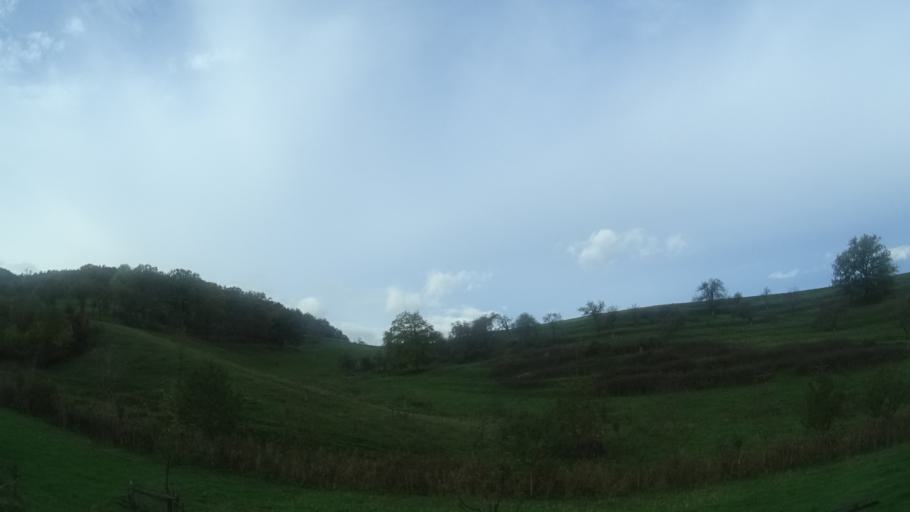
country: DE
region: Thuringia
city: Saalfeld
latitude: 50.6932
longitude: 11.3815
